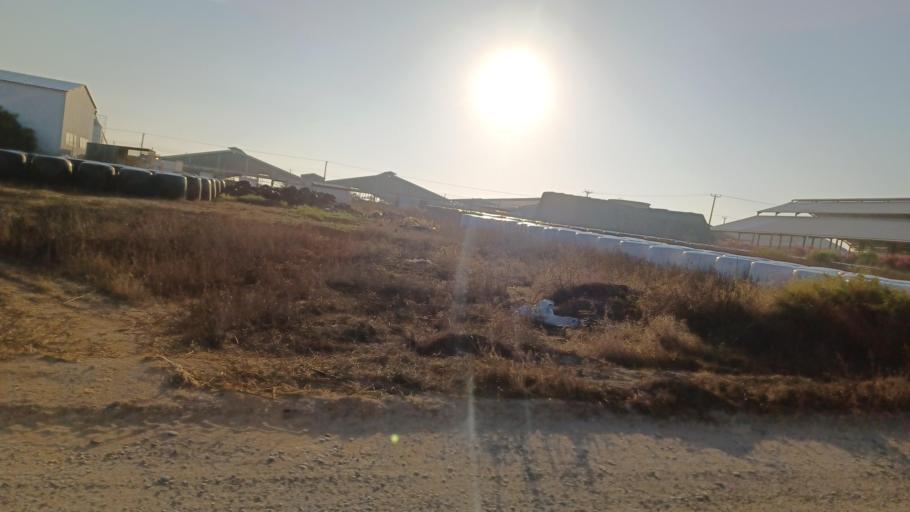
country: CY
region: Ammochostos
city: Achna
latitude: 35.0181
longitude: 33.7994
